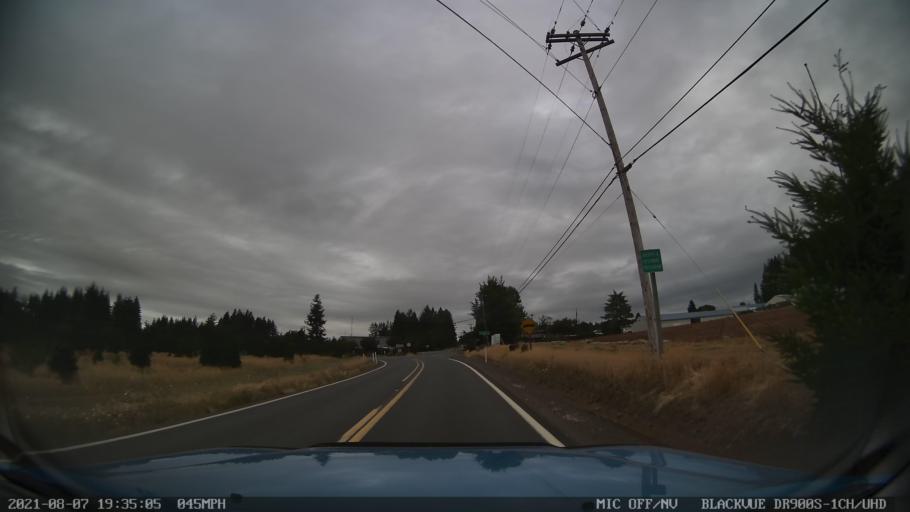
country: US
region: Oregon
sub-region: Marion County
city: Silverton
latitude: 44.9249
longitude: -122.6567
